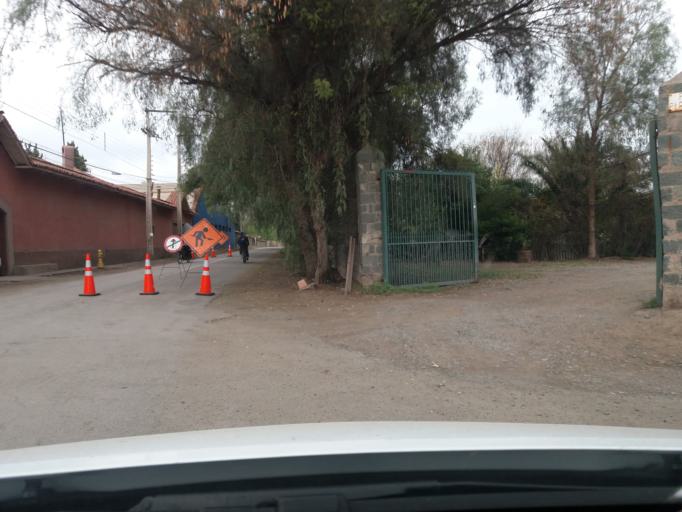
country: CL
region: Valparaiso
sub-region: Provincia de Los Andes
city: Los Andes
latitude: -32.8250
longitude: -70.6475
